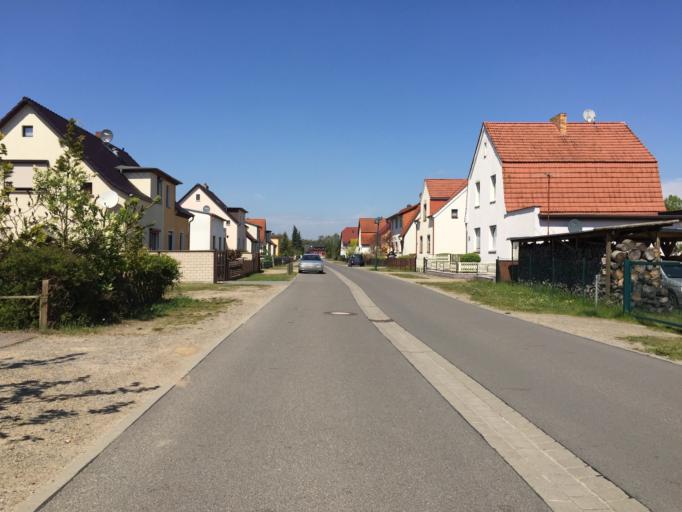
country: DE
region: Brandenburg
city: Marienwerder
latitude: 52.8480
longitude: 13.6752
